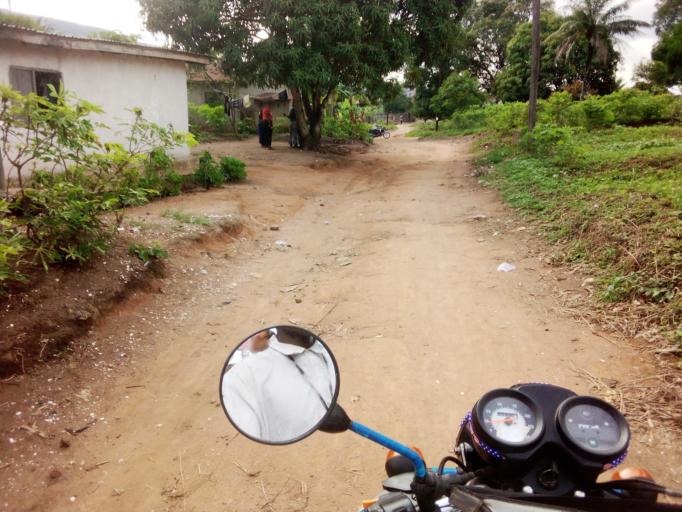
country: SL
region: Western Area
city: Waterloo
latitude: 8.3439
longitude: -13.0689
